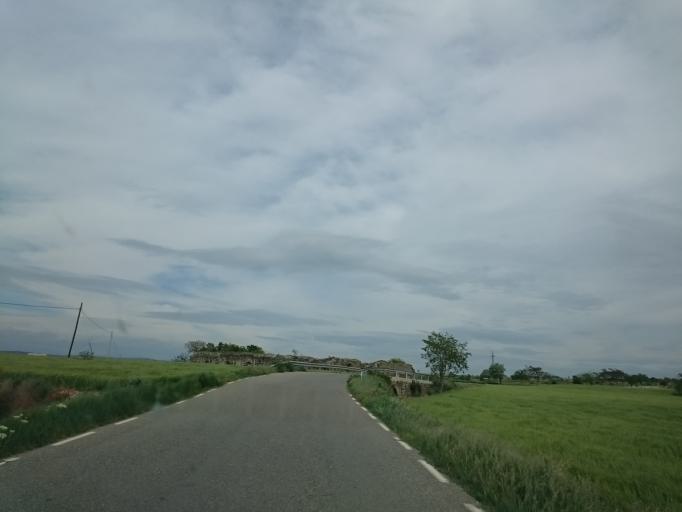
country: ES
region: Catalonia
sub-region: Provincia de Lleida
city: Ivorra
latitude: 41.7883
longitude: 1.2982
